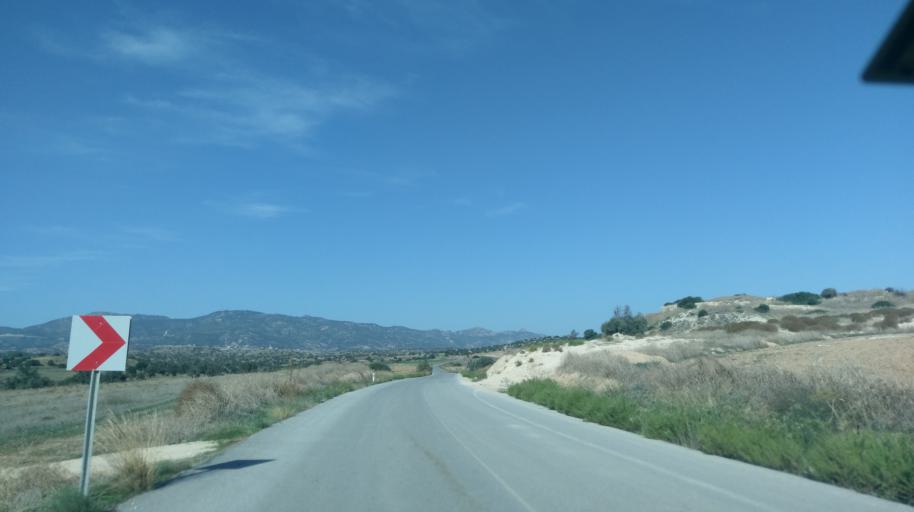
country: CY
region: Ammochostos
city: Trikomo
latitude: 35.3164
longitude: 33.8927
